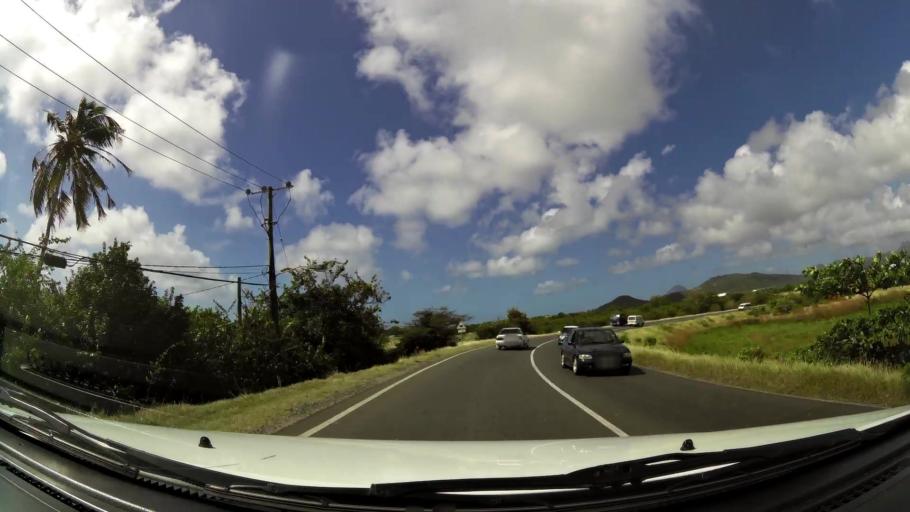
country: LC
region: Laborie Quarter
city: Laborie
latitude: 13.7313
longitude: -60.9694
